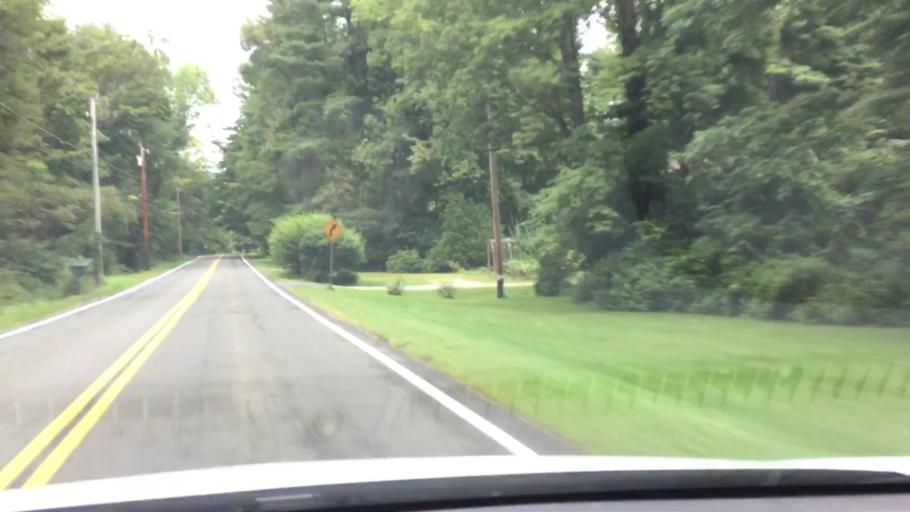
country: US
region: Massachusetts
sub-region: Berkshire County
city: Housatonic
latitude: 42.2379
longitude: -73.3719
